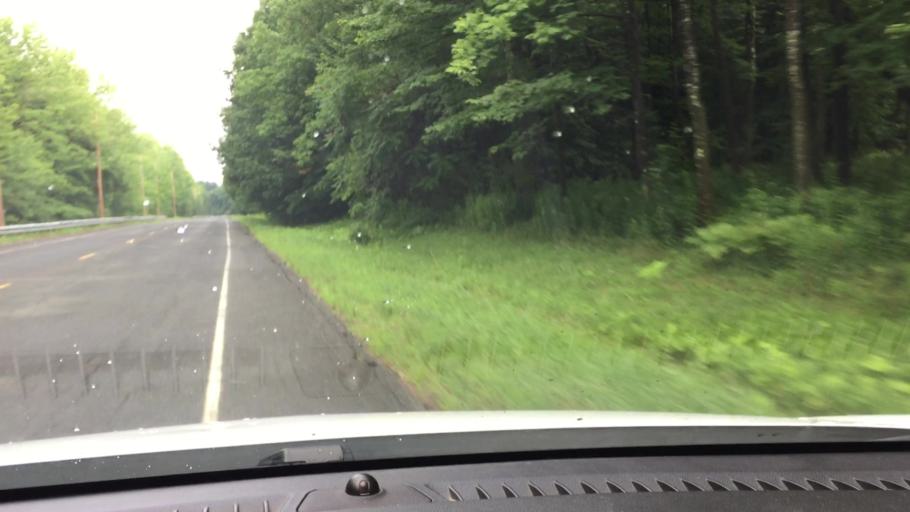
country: US
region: Massachusetts
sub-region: Berkshire County
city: Hinsdale
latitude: 42.4260
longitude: -73.0044
